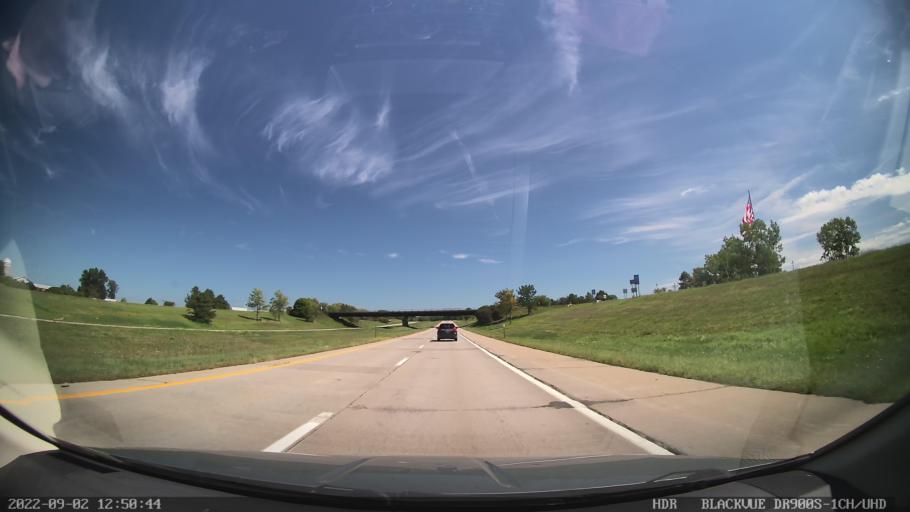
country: US
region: New York
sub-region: Livingston County
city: Avon
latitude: 42.8678
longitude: -77.7157
